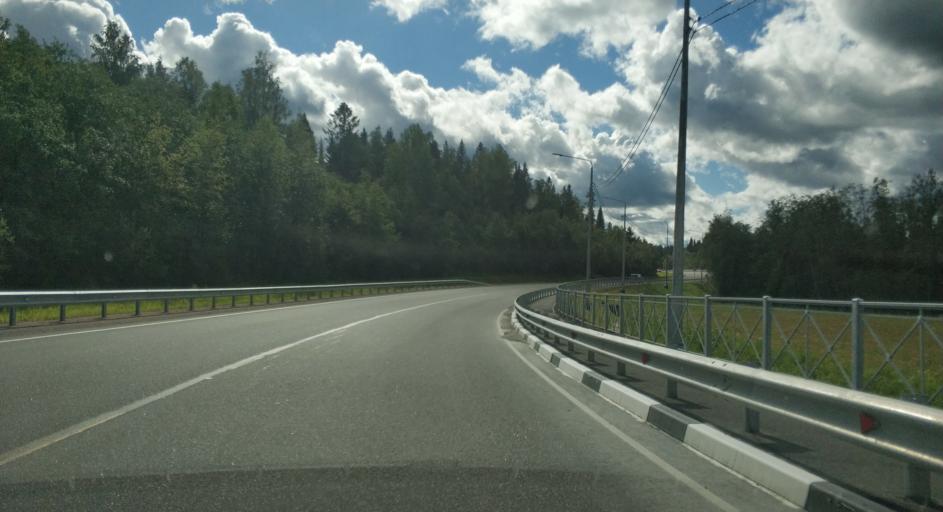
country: RU
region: Republic of Karelia
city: Ruskeala
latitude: 61.9458
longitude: 30.5984
